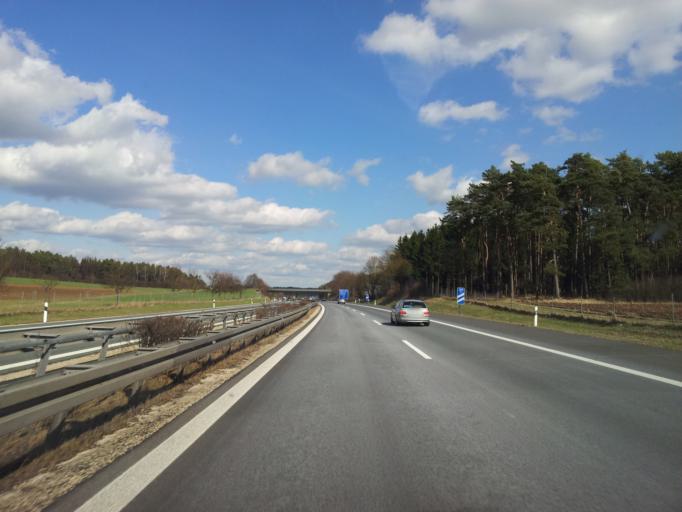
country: DE
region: Bavaria
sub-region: Upper Franconia
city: Wattendorf
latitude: 49.9874
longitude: 11.1145
